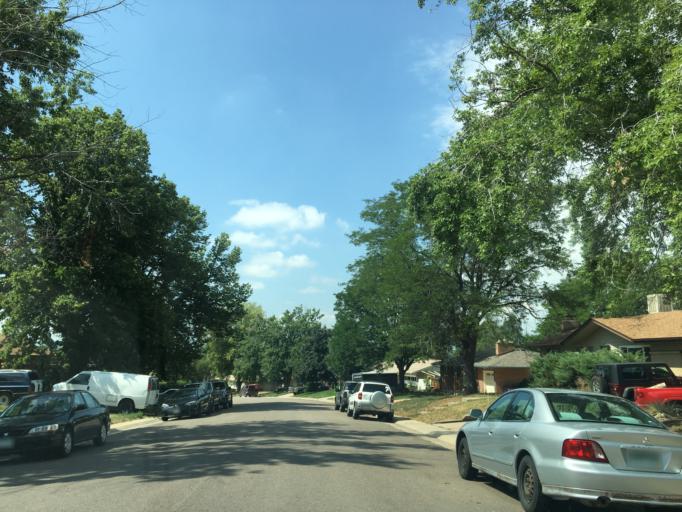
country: US
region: Colorado
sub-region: Arapahoe County
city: Sheridan
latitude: 39.6646
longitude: -105.0457
